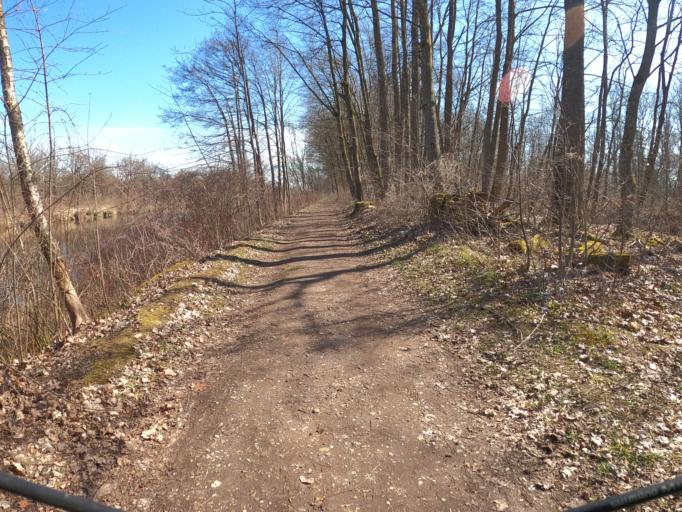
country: DE
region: Bavaria
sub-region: Swabia
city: Nersingen
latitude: 48.4408
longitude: 10.1191
